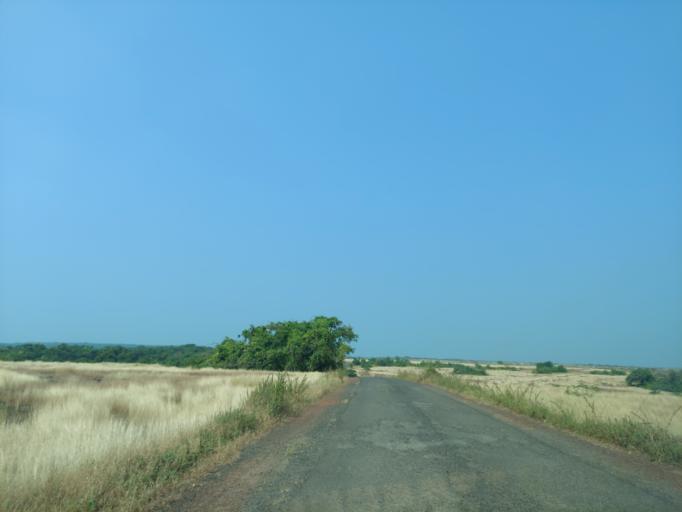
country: IN
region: Maharashtra
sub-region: Sindhudurg
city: Malvan
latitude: 15.9959
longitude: 73.5201
